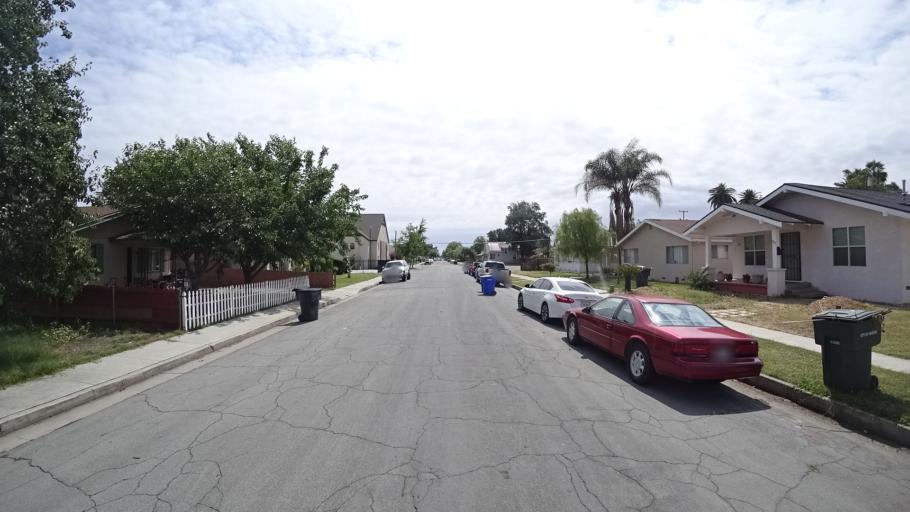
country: US
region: California
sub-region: Kings County
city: Hanford
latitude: 36.3340
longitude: -119.6505
